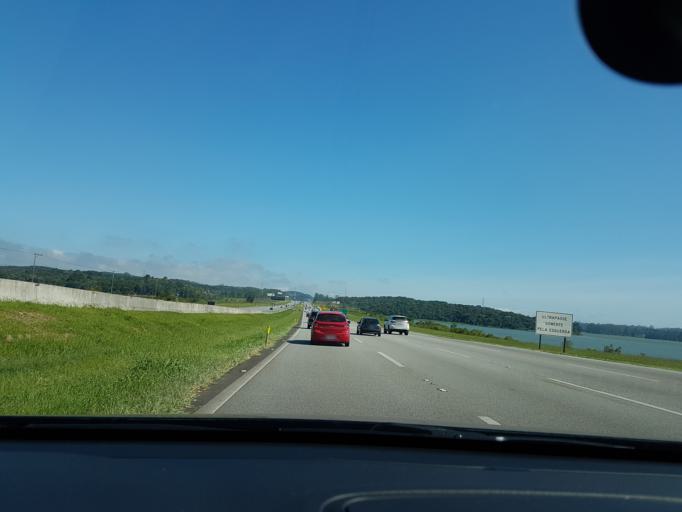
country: BR
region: Sao Paulo
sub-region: Sao Bernardo Do Campo
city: Sao Bernardo do Campo
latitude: -23.7888
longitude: -46.5971
